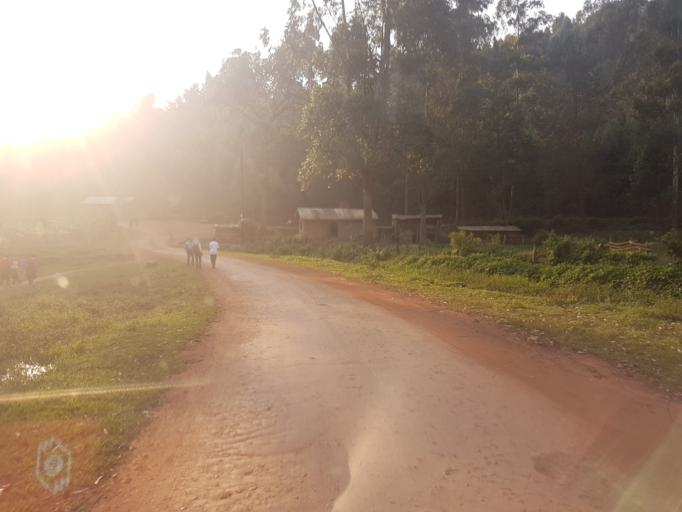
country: UG
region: Western Region
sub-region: Kabale District
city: Kabale
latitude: -1.1236
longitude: 29.9073
